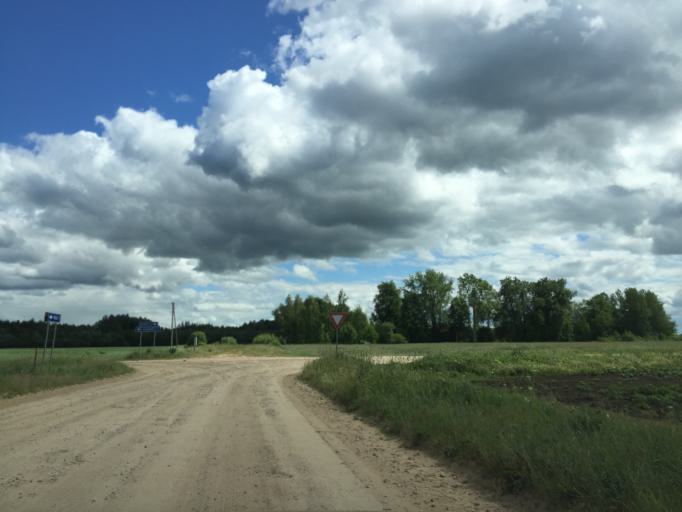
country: LV
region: Lecava
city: Iecava
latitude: 56.5002
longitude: 24.3606
